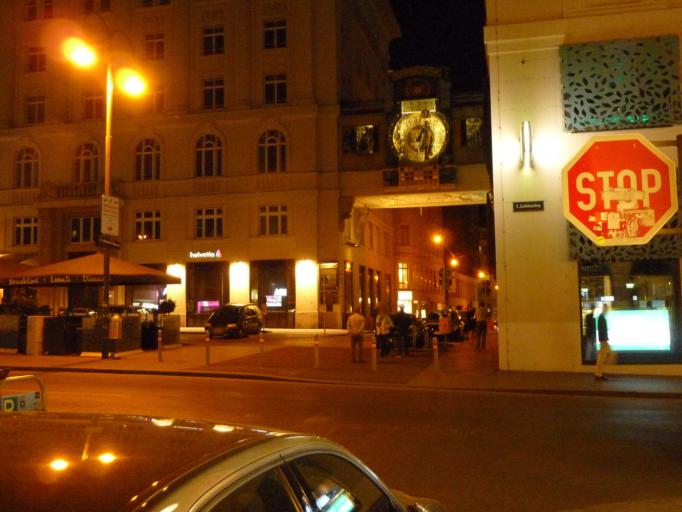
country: AT
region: Vienna
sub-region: Wien Stadt
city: Vienna
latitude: 48.2104
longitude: 16.3734
